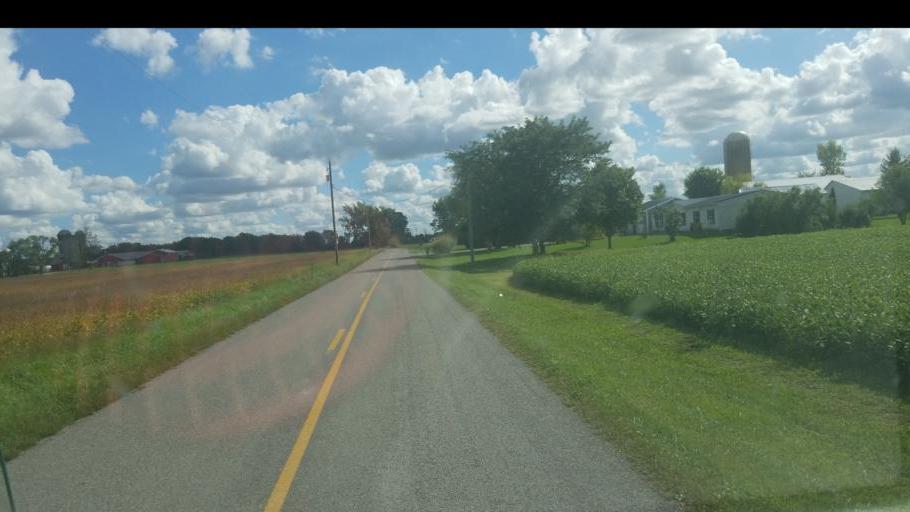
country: US
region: Ohio
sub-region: Hardin County
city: Kenton
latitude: 40.5053
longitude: -83.5507
